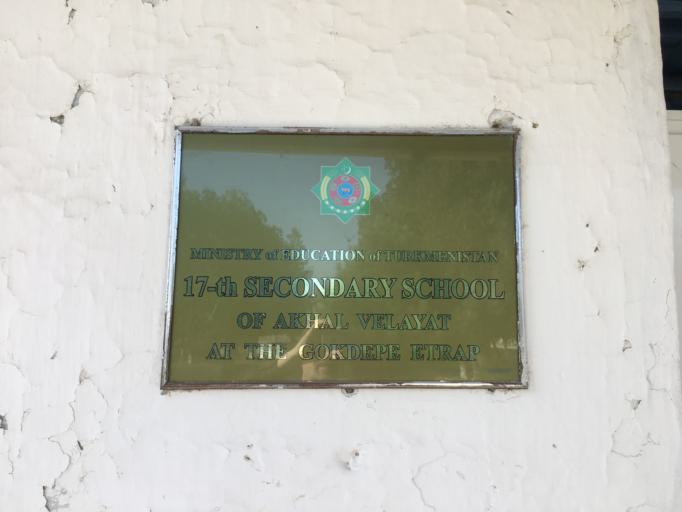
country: TM
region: Ahal
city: Arcabil
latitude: 38.1070
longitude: 57.9776
